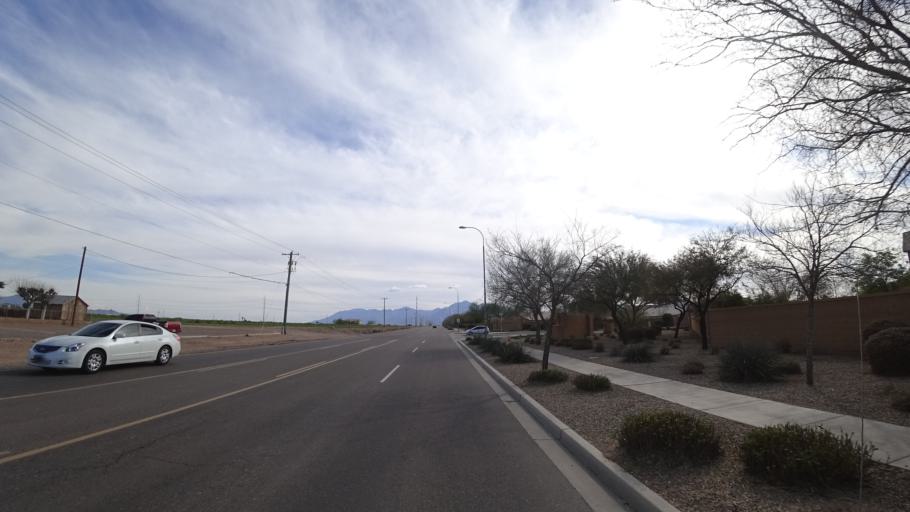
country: US
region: Arizona
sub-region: Maricopa County
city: Tolleson
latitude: 33.4107
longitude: -112.2725
